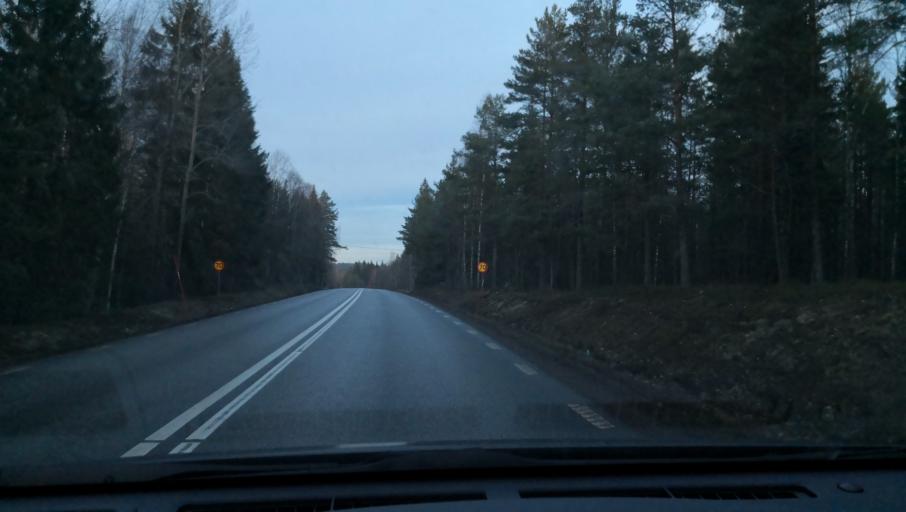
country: SE
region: OErebro
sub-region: Laxa Kommun
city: Laxa
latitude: 59.1432
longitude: 14.6823
